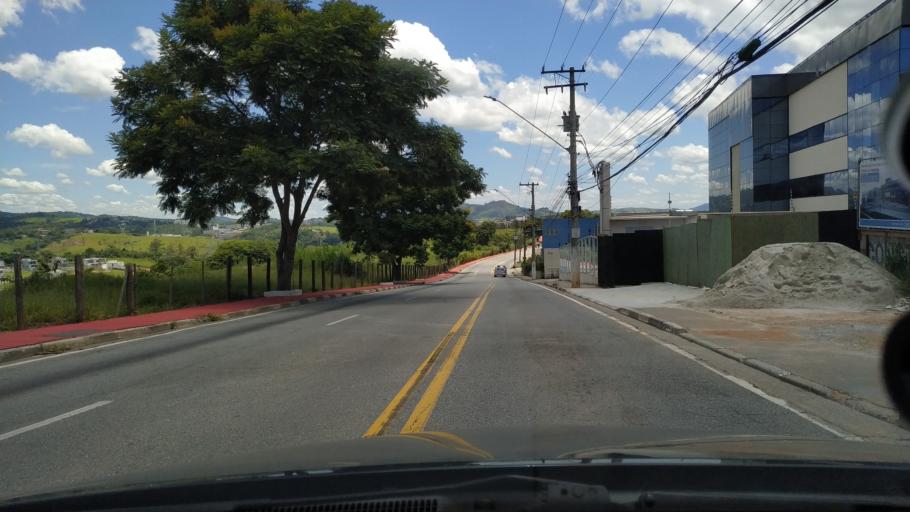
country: BR
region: Sao Paulo
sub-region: Santana De Parnaiba
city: Santana de Parnaiba
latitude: -23.4532
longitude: -46.8975
